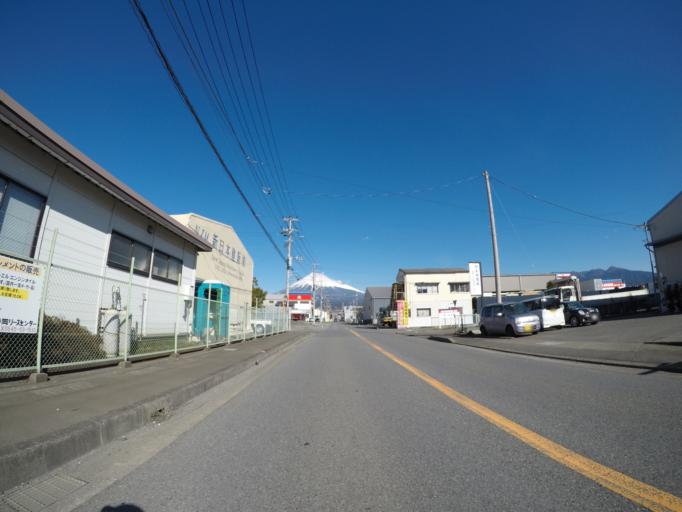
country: JP
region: Shizuoka
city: Fuji
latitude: 35.1518
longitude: 138.7013
